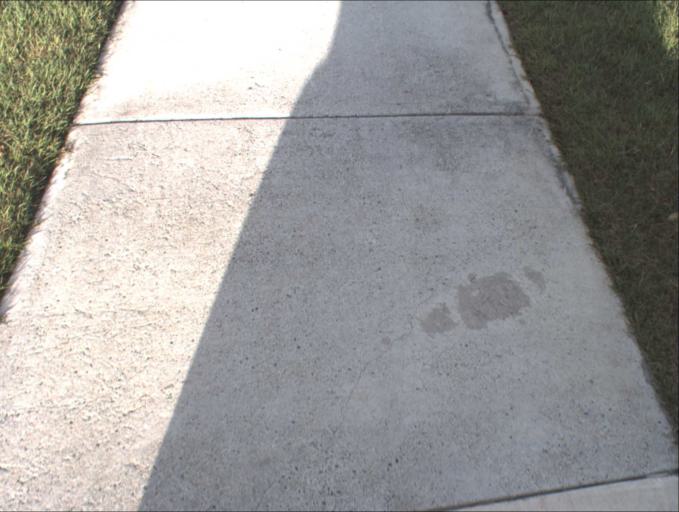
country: AU
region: Queensland
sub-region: Logan
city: North Maclean
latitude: -27.8037
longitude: 152.9590
